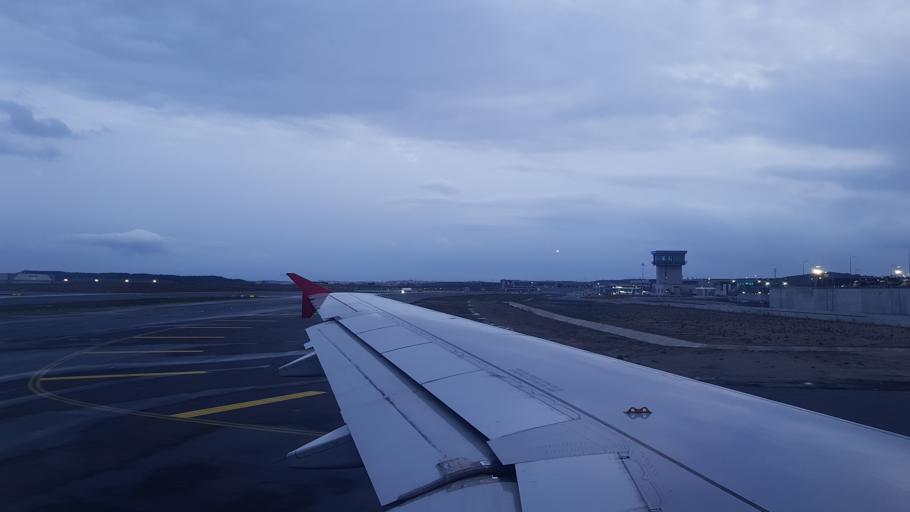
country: TR
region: Istanbul
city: Durusu
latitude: 41.2651
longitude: 28.7211
